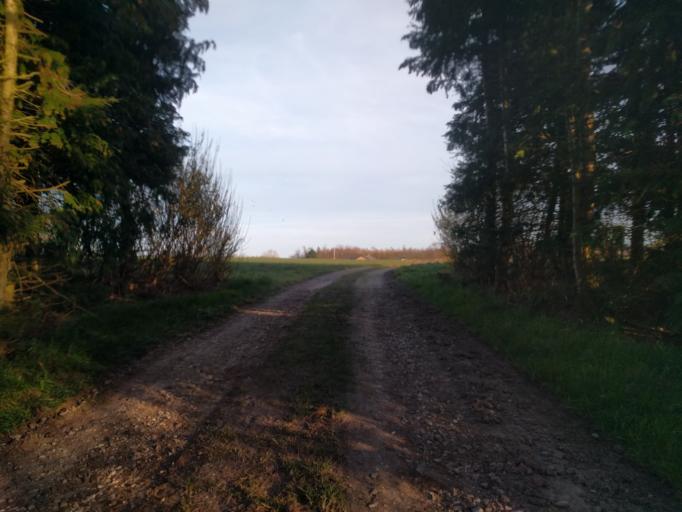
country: DK
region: South Denmark
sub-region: Kerteminde Kommune
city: Langeskov
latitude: 55.3769
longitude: 10.5732
